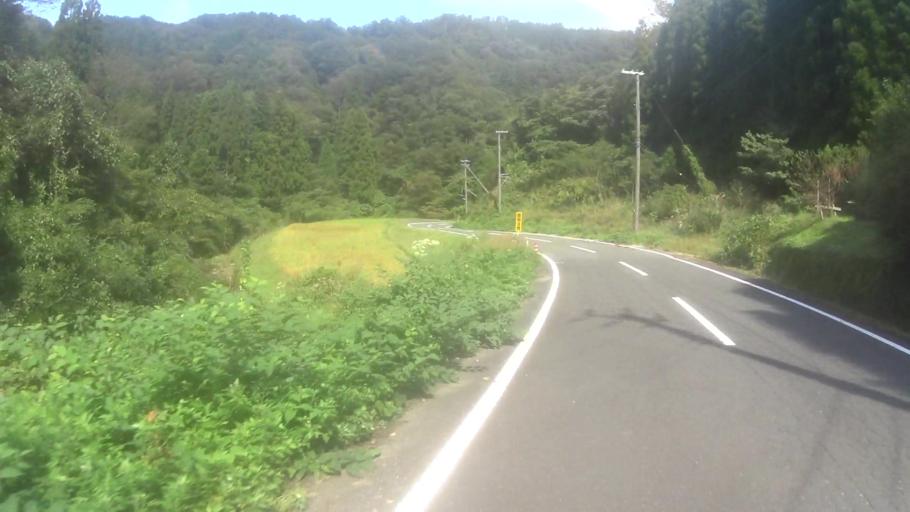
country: JP
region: Kyoto
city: Miyazu
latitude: 35.6767
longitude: 135.1542
